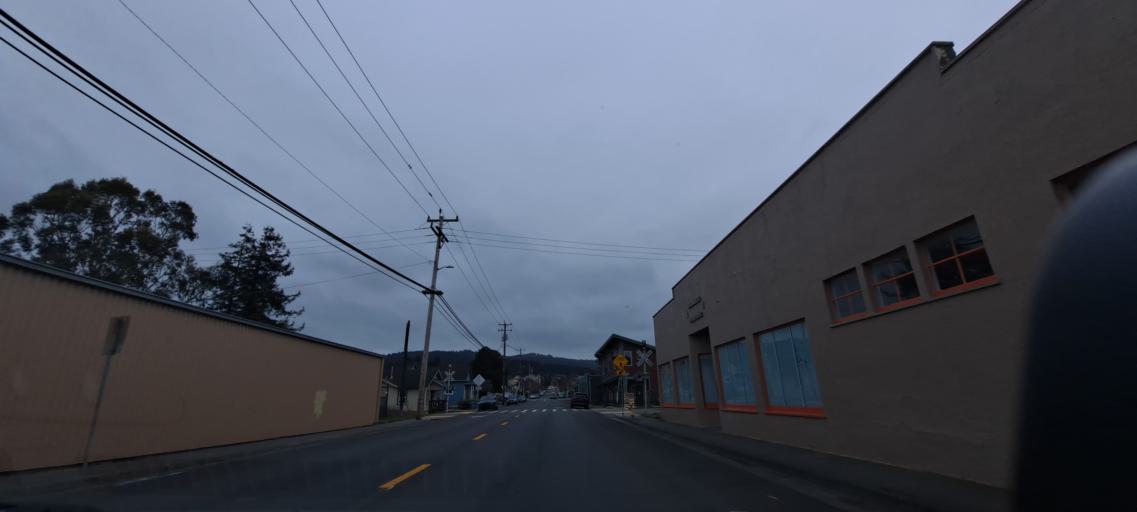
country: US
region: California
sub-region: Humboldt County
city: Arcata
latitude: 40.8717
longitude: -124.0913
